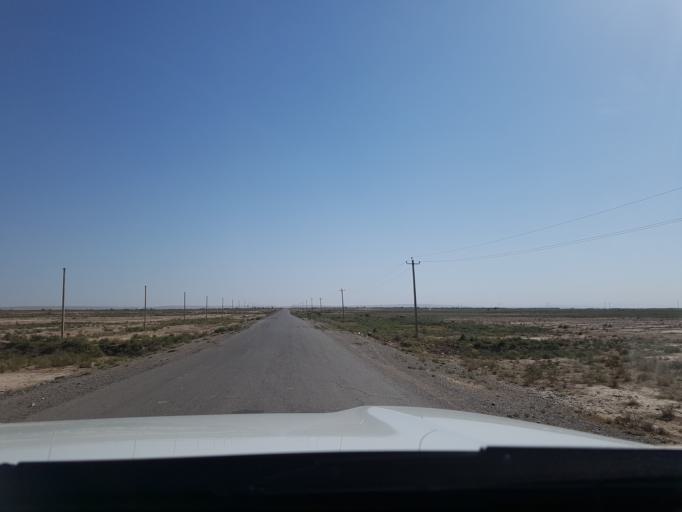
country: IR
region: Razavi Khorasan
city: Sarakhs
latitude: 36.5089
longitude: 61.2532
